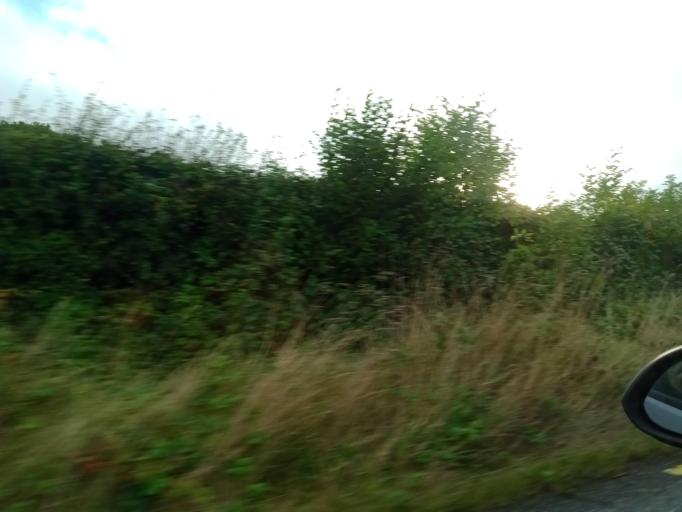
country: IE
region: Leinster
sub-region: Laois
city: Mountmellick
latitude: 53.1385
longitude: -7.4170
